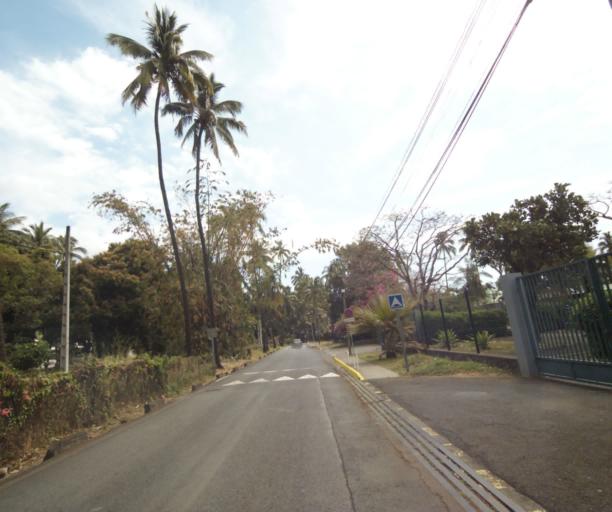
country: RE
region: Reunion
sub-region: Reunion
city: Saint-Paul
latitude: -21.0105
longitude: 55.2834
